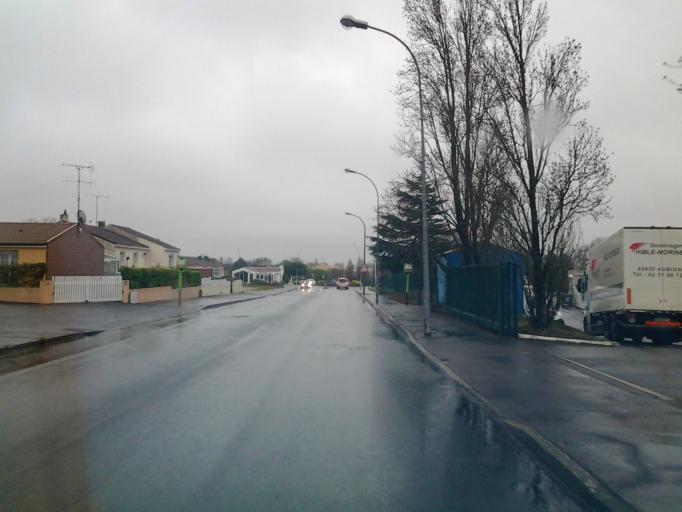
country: FR
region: Pays de la Loire
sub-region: Departement de la Vendee
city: La Roche-sur-Yon
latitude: 46.6649
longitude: -1.4558
